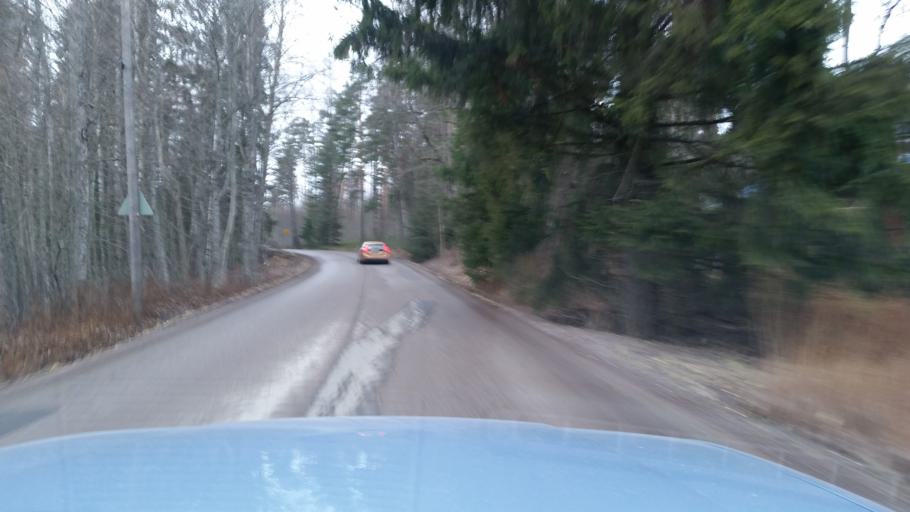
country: FI
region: Uusimaa
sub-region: Helsinki
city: Kauniainen
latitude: 60.2718
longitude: 24.6896
